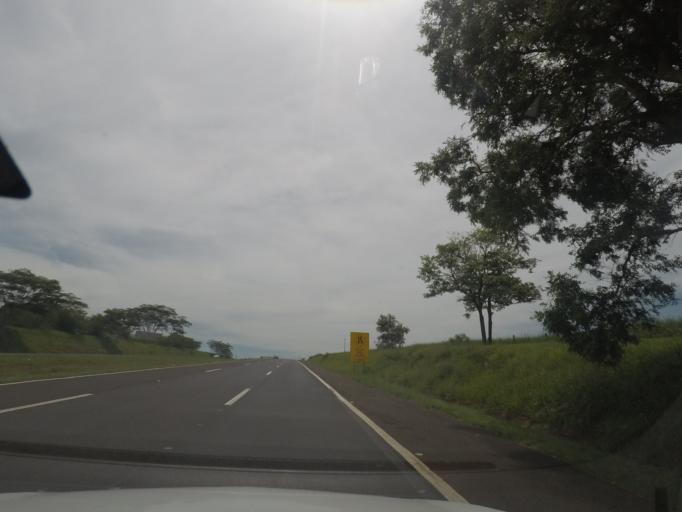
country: BR
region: Sao Paulo
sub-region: Bebedouro
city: Bebedouro
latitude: -20.9686
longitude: -48.4407
